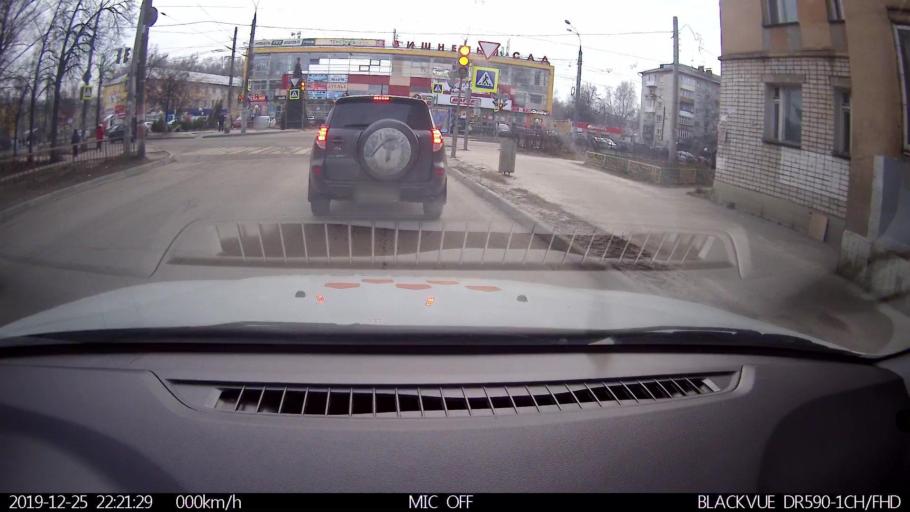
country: RU
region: Nizjnij Novgorod
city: Gorbatovka
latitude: 56.3318
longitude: 43.8401
